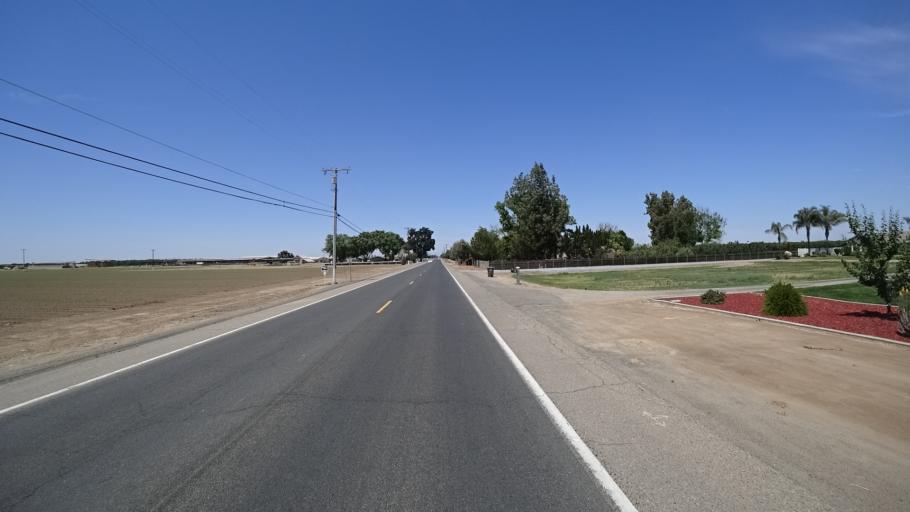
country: US
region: California
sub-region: Kings County
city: Armona
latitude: 36.3427
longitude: -119.7195
